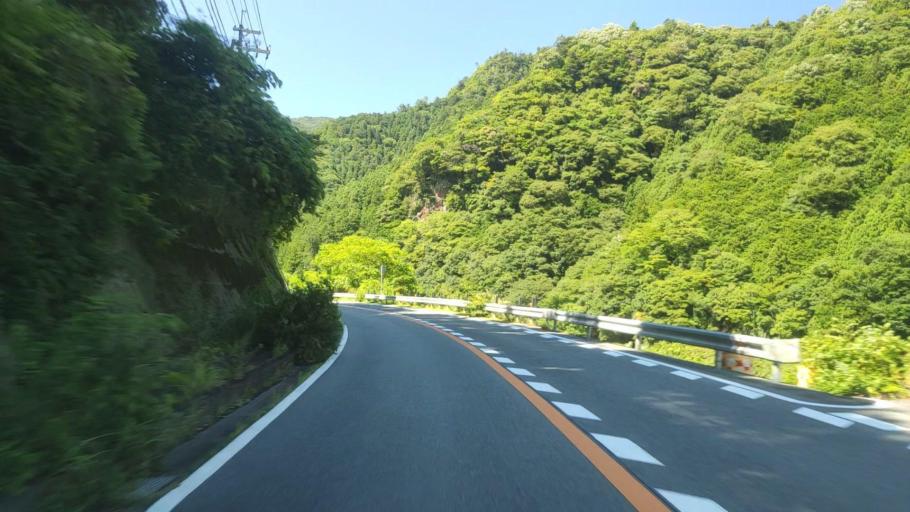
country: JP
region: Nara
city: Yoshino-cho
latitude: 34.3103
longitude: 135.9930
